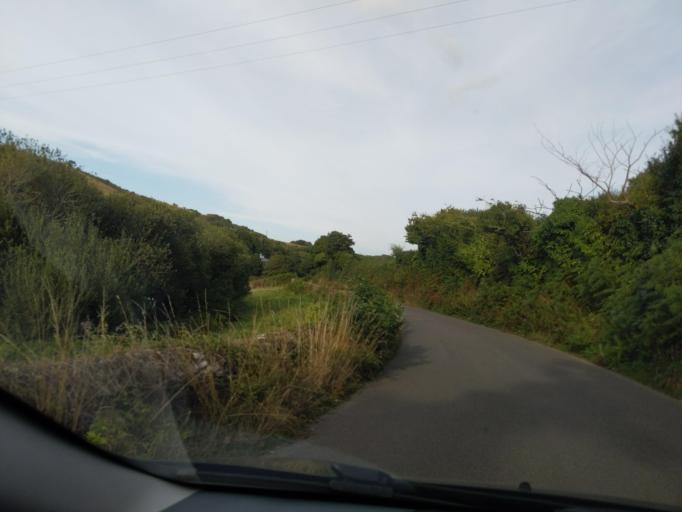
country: GB
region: England
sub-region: Cornwall
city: Millbrook
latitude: 50.3300
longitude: -4.2093
